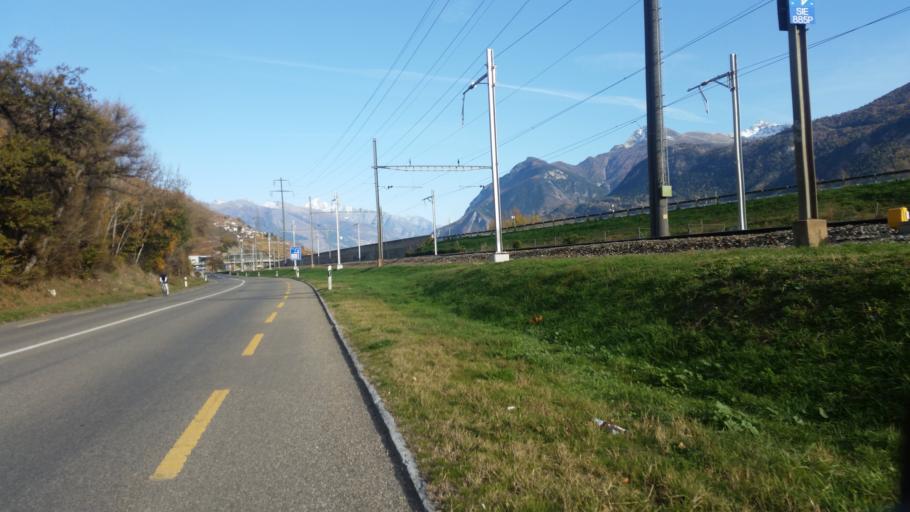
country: CH
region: Valais
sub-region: Sierre District
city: Grone
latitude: 46.2633
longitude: 7.4533
